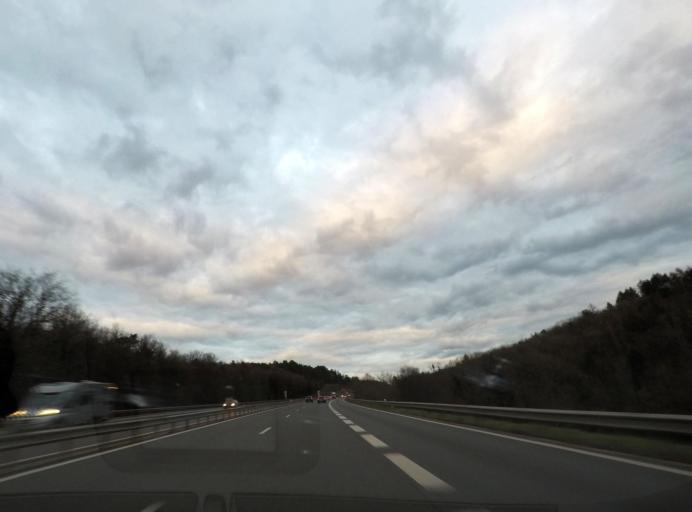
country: FR
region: Rhone-Alpes
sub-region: Departement de l'Ain
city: Poncin
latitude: 46.0987
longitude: 5.4292
